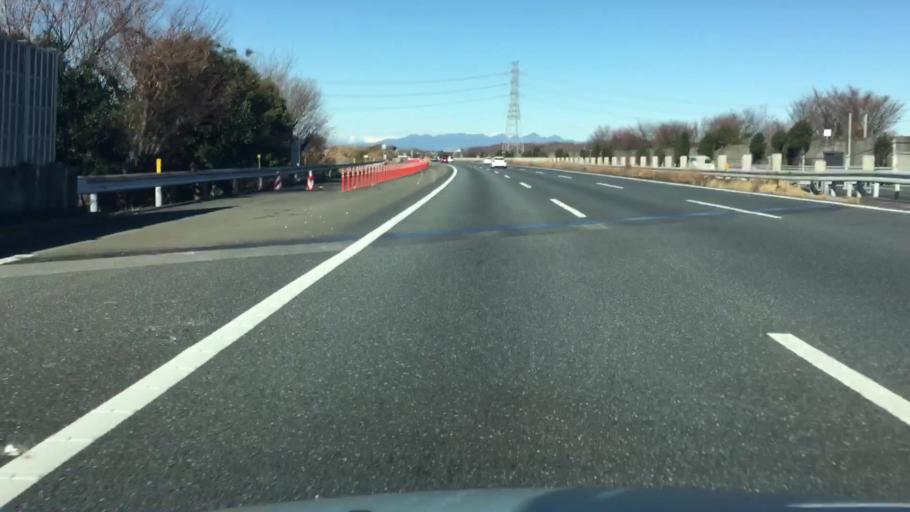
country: JP
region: Saitama
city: Honjo
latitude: 36.1991
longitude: 139.1836
